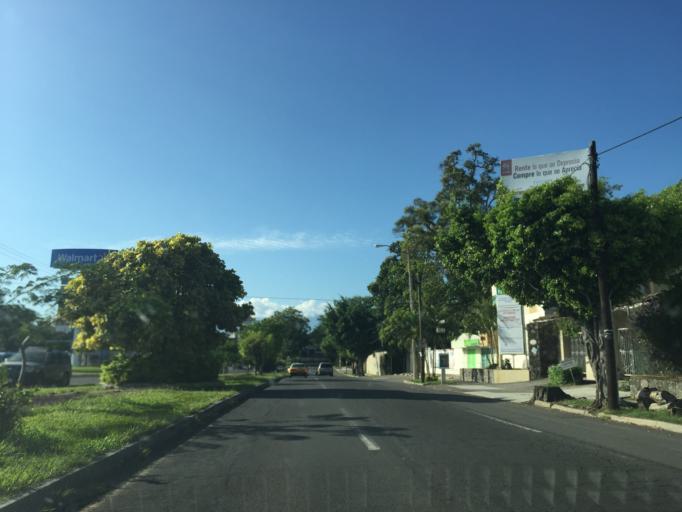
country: MX
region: Colima
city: Colima
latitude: 19.2586
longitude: -103.7198
